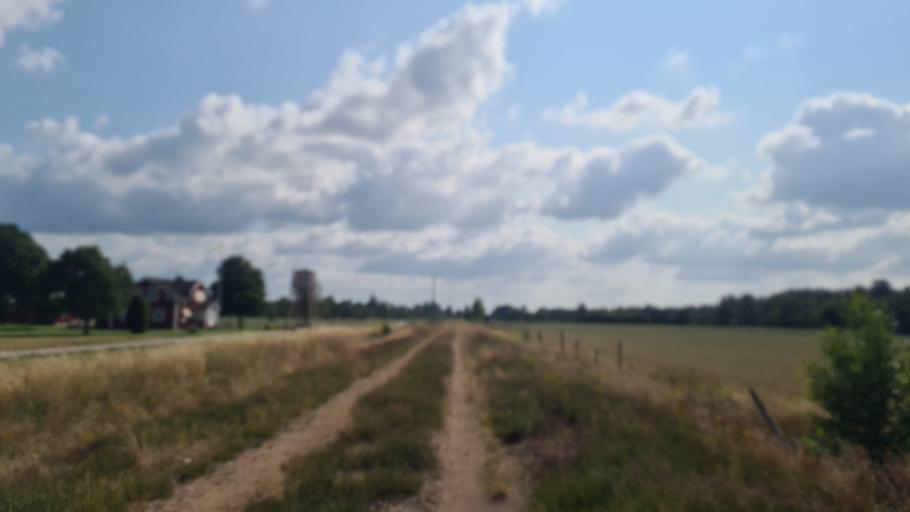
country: SE
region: Kronoberg
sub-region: Ljungby Kommun
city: Ljungby
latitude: 56.7539
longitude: 13.8851
